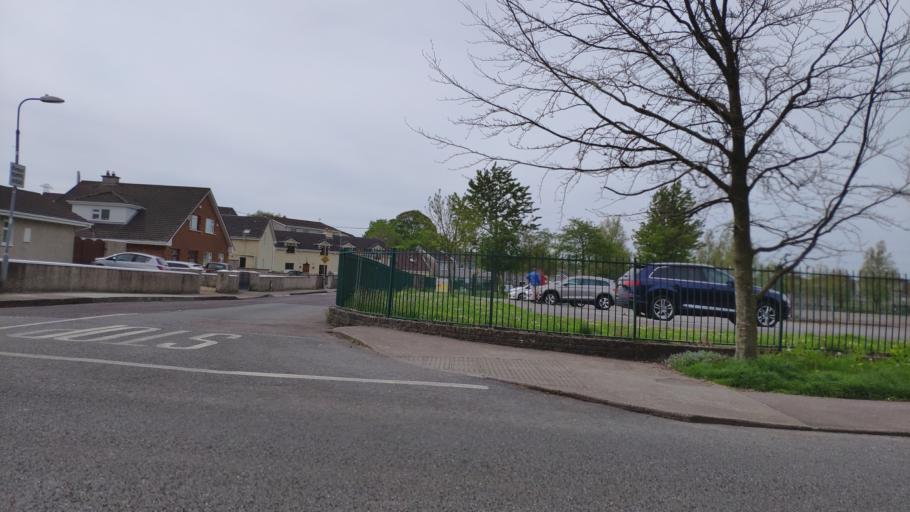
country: IE
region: Munster
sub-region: County Cork
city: Cork
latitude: 51.9197
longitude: -8.4527
